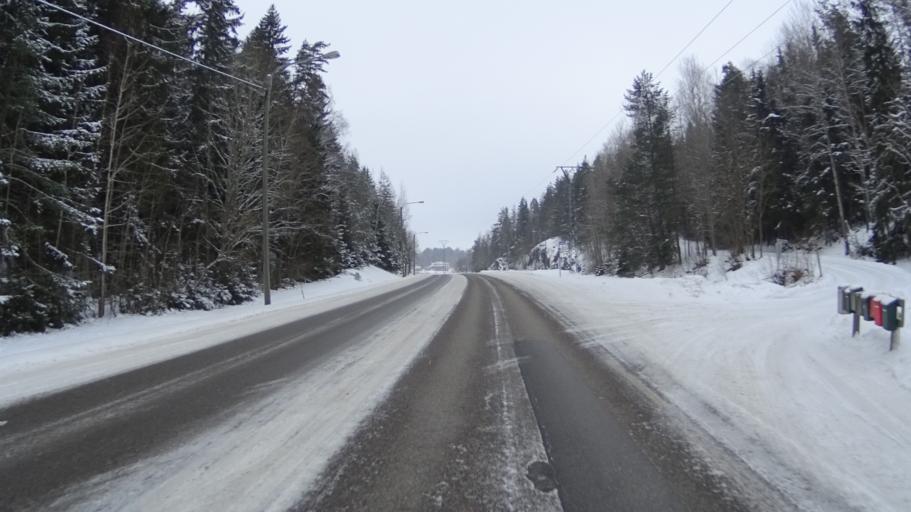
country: FI
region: Uusimaa
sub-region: Helsinki
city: Vihti
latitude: 60.3589
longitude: 24.1759
